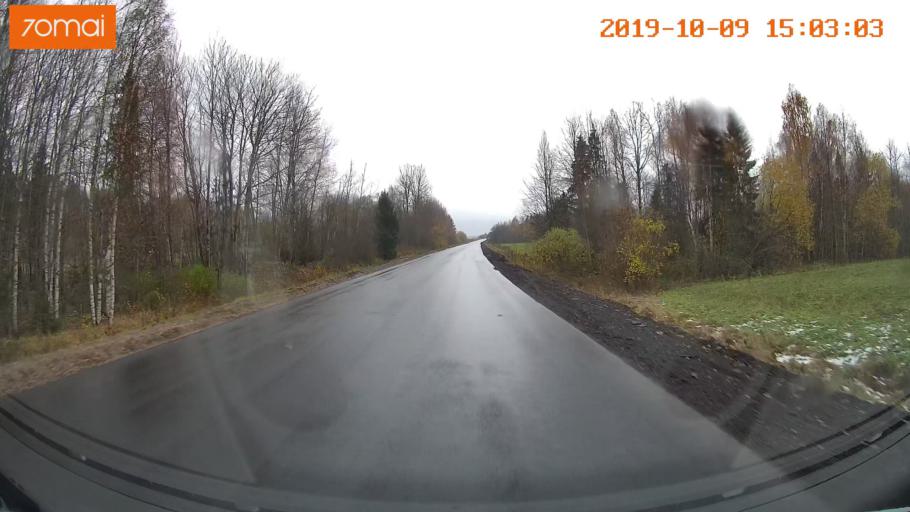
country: RU
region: Kostroma
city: Chistyye Bory
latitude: 58.2767
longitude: 41.6763
